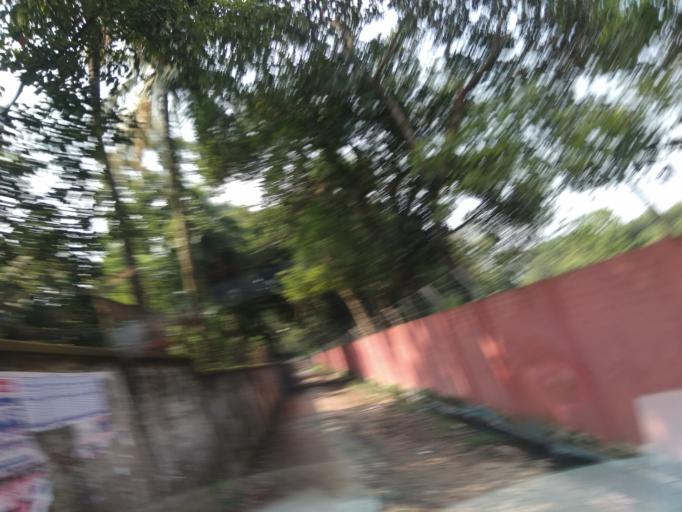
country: BD
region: Rangpur Division
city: Rangpur
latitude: 25.7579
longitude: 89.2370
